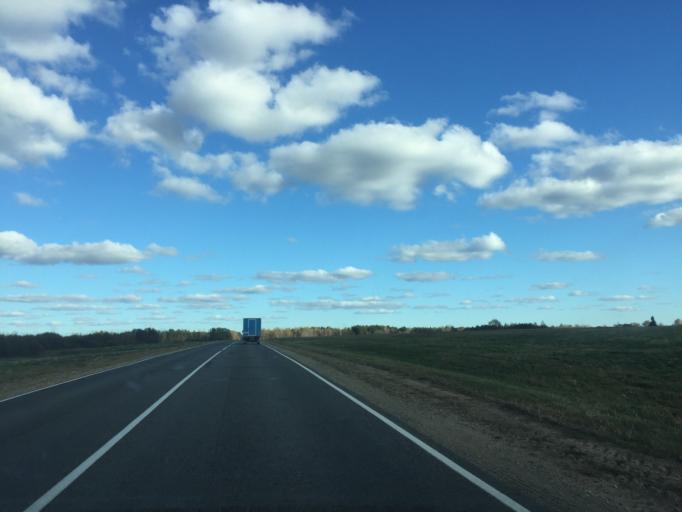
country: BY
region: Minsk
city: Myadzyel
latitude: 55.0440
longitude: 27.0489
